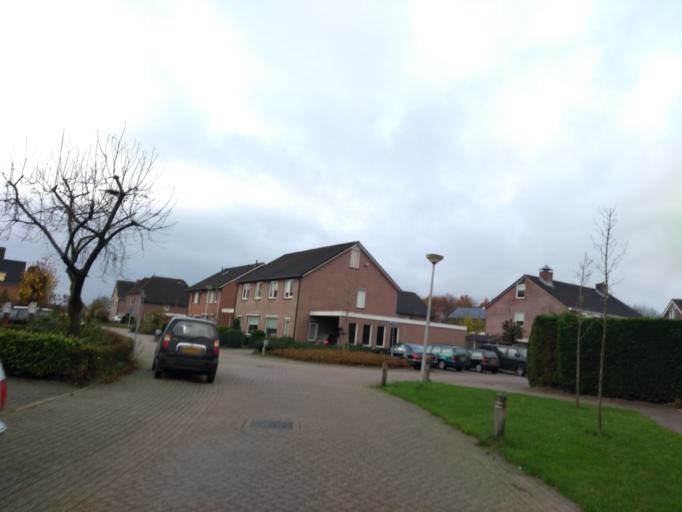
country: NL
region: Overijssel
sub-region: Gemeente Almelo
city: Almelo
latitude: 52.3811
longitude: 6.7075
